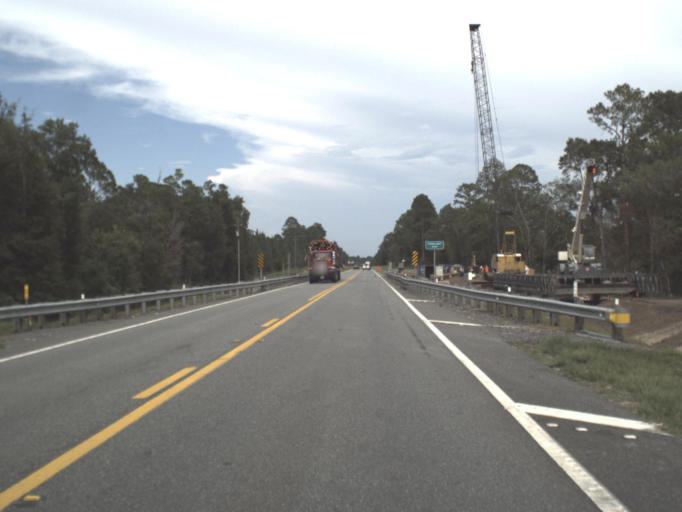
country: US
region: Florida
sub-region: Taylor County
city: Perry
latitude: 30.0981
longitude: -83.4729
